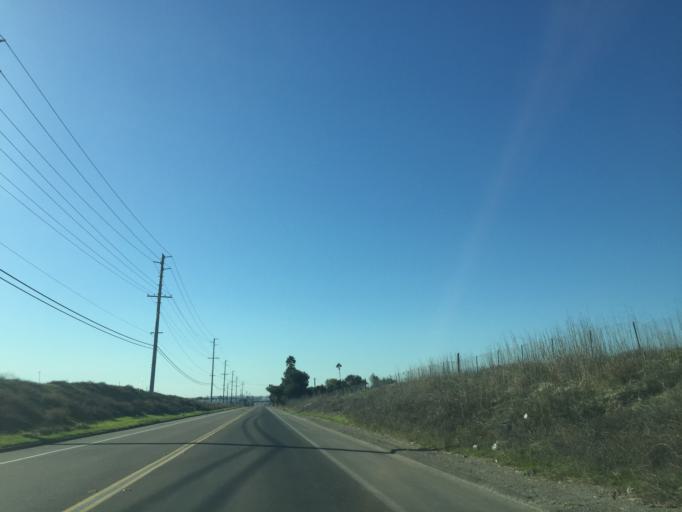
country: MX
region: Baja California
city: Tijuana
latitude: 32.5675
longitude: -116.9310
